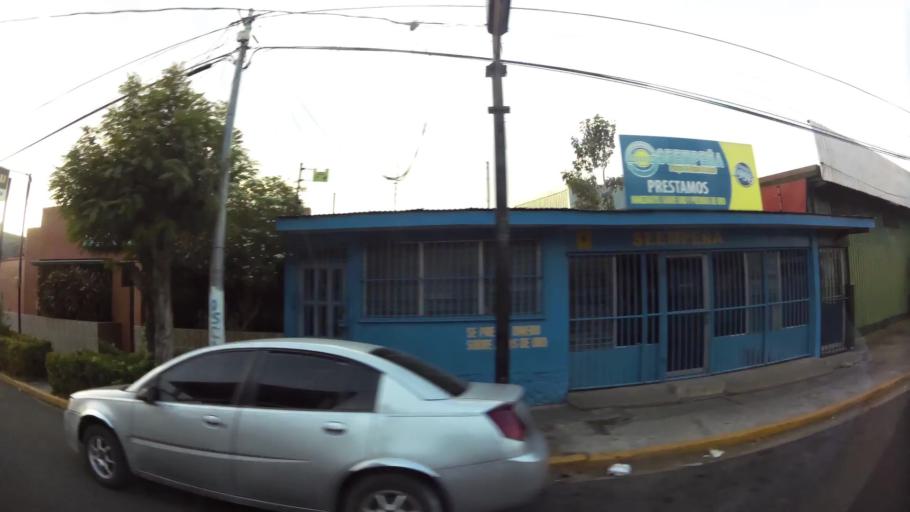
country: NI
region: Managua
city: Managua
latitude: 12.1463
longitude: -86.2553
